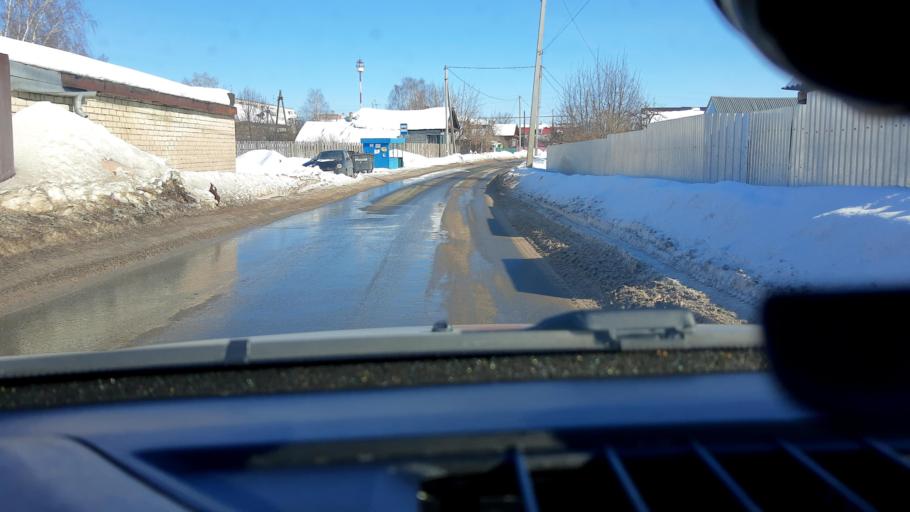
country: RU
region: Nizjnij Novgorod
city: Volodarsk
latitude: 56.2365
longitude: 43.1880
